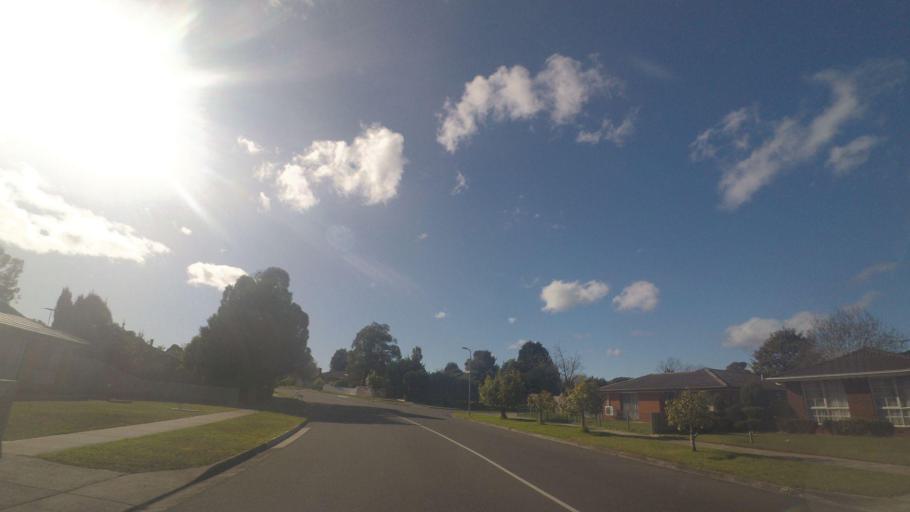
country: AU
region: Victoria
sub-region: Knox
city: Scoresby
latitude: -37.9165
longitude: 145.2509
